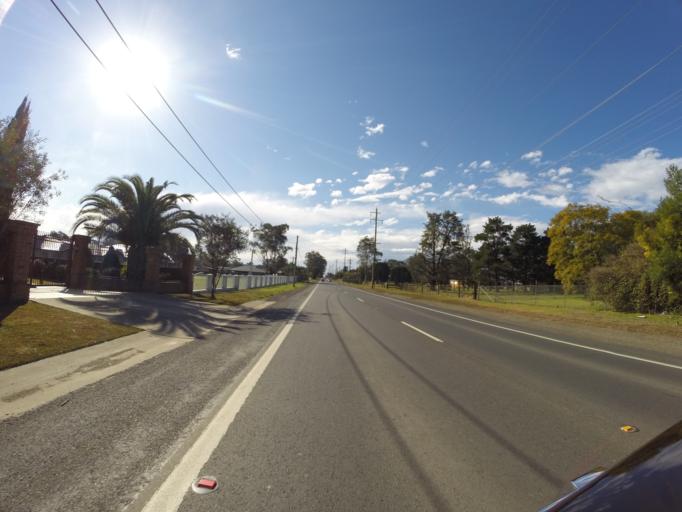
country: AU
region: New South Wales
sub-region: Liverpool
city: Bringelly
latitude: -33.9055
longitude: 150.7880
